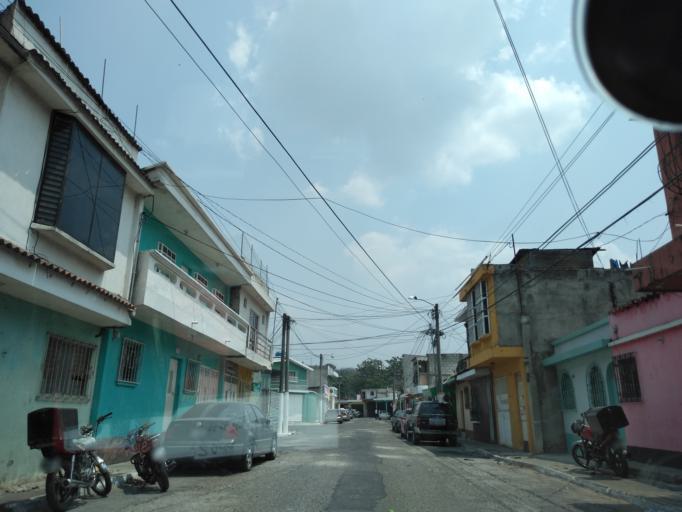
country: GT
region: Guatemala
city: Petapa
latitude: 14.5246
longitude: -90.5415
